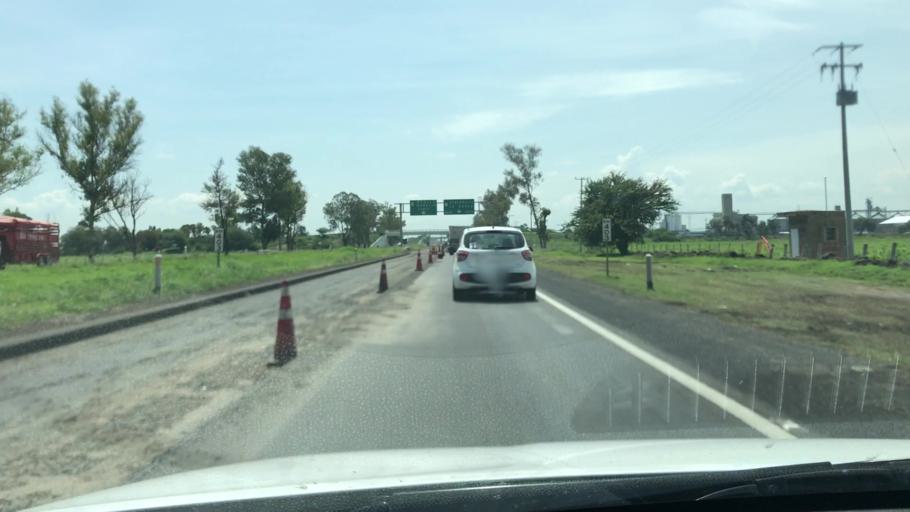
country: MX
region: Jalisco
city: La Barca
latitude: 20.3220
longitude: -102.5448
